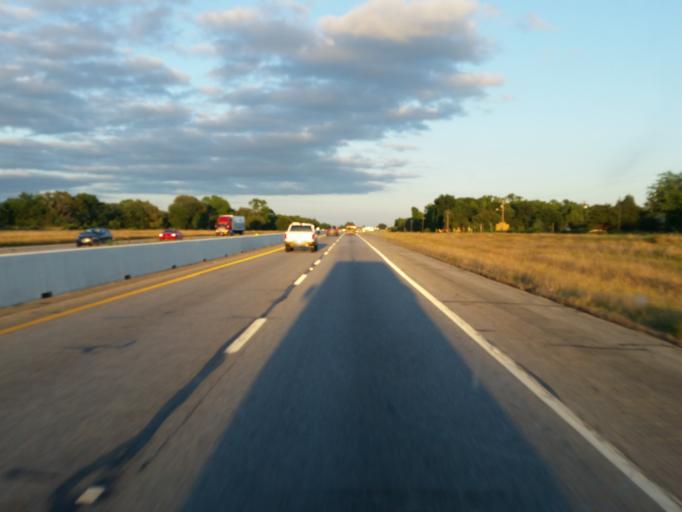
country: US
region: Texas
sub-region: Van Zandt County
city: Van
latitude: 32.5330
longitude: -95.7310
